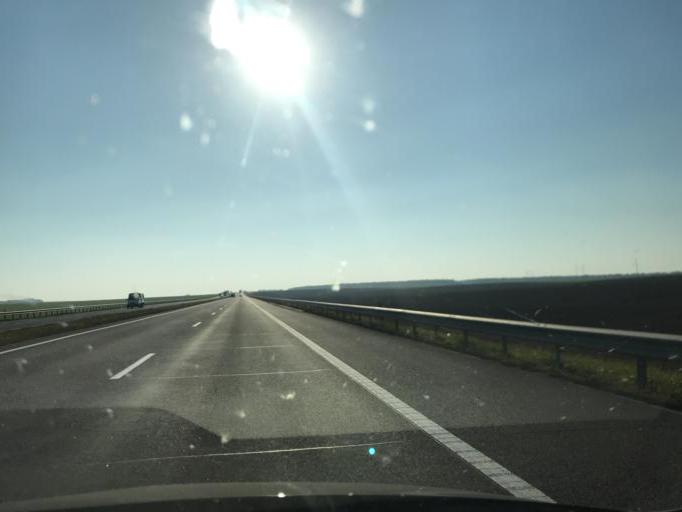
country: BY
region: Grodnenskaya
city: Mir
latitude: 53.4336
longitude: 26.5860
